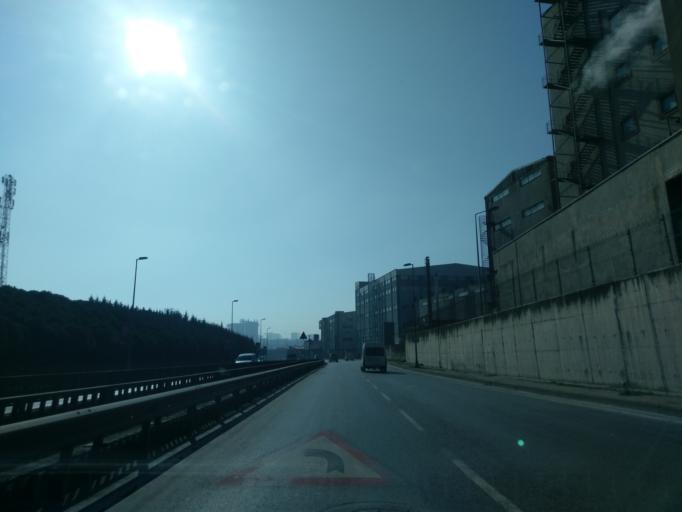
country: TR
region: Istanbul
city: Basaksehir
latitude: 41.0786
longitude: 28.8124
